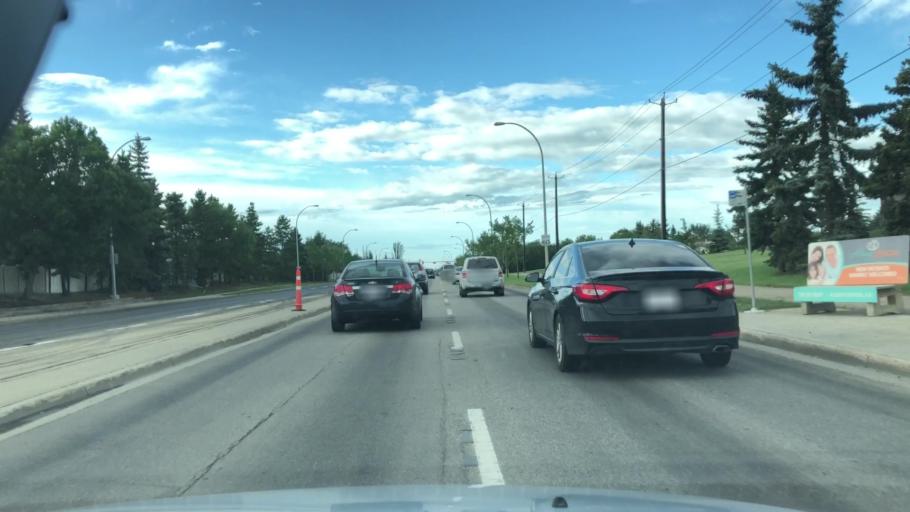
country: CA
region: Alberta
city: St. Albert
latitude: 53.6205
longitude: -113.5411
